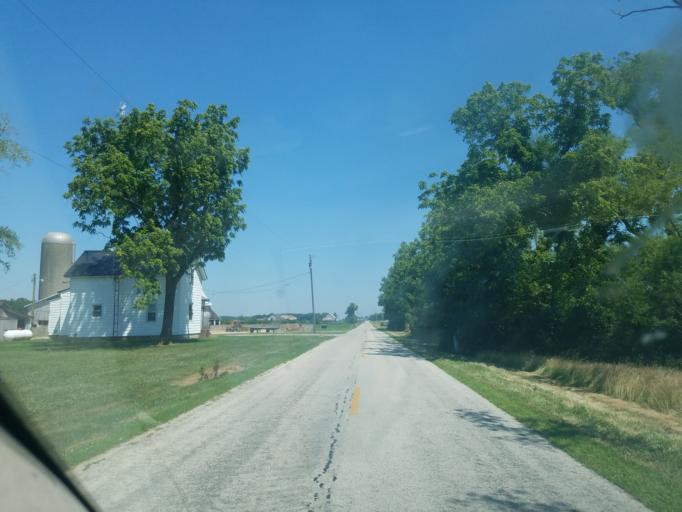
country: US
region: Ohio
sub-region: Mercer County
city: Coldwater
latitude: 40.5714
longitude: -84.7083
